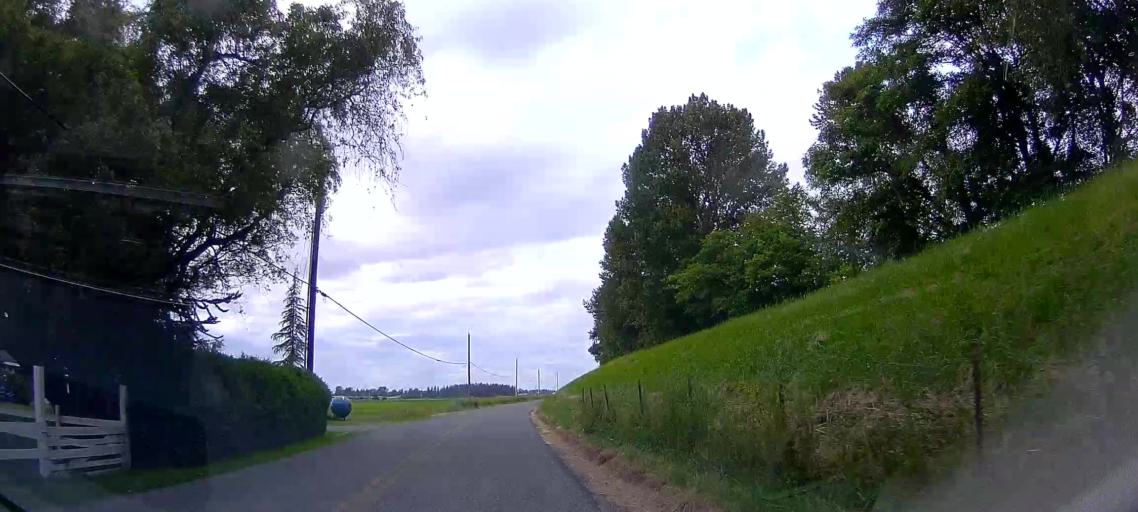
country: US
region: Washington
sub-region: Skagit County
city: Mount Vernon
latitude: 48.3509
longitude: -122.3623
